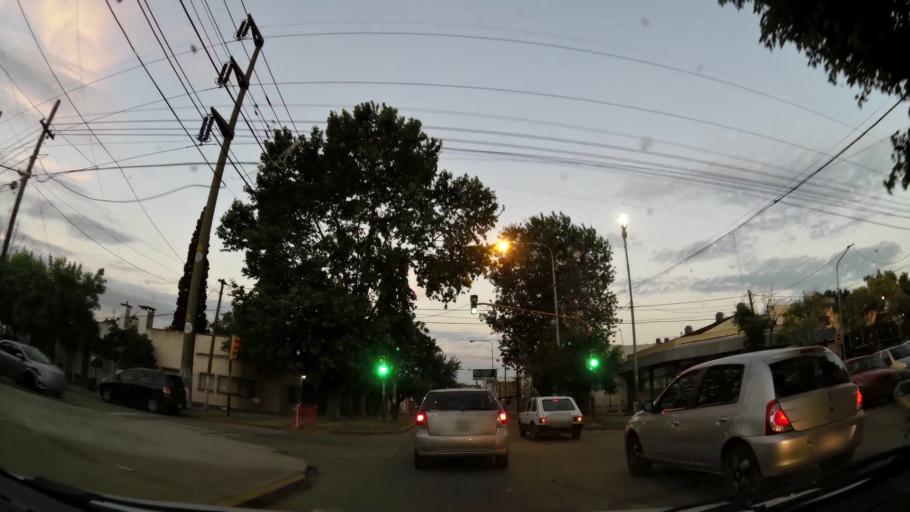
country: AR
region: Buenos Aires
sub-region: Partido de Merlo
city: Merlo
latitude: -34.6653
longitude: -58.7349
